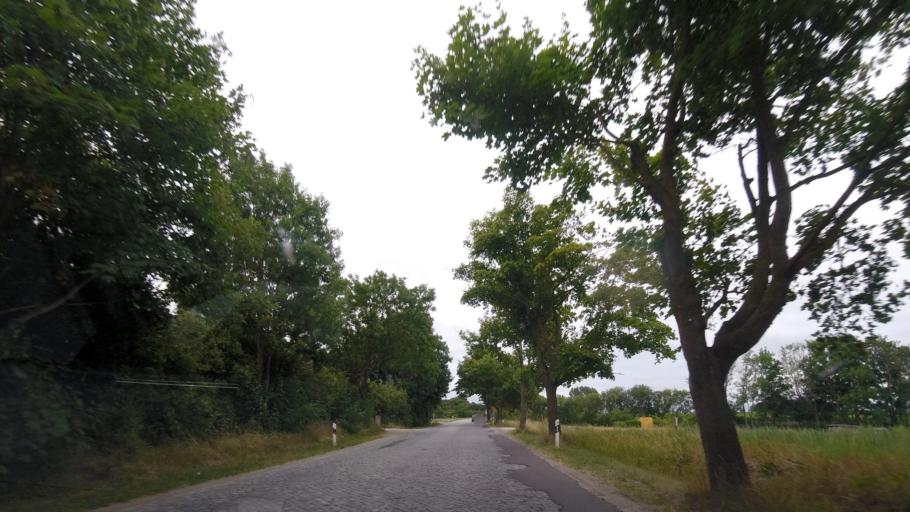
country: DE
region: Mecklenburg-Vorpommern
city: Sagard
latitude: 54.5238
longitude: 13.5465
